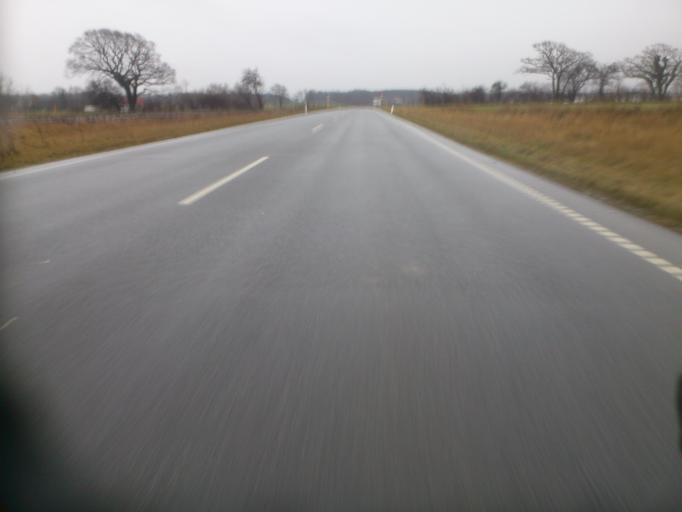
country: DK
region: South Denmark
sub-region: Fredericia Kommune
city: Snoghoj
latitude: 55.5712
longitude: 9.6906
